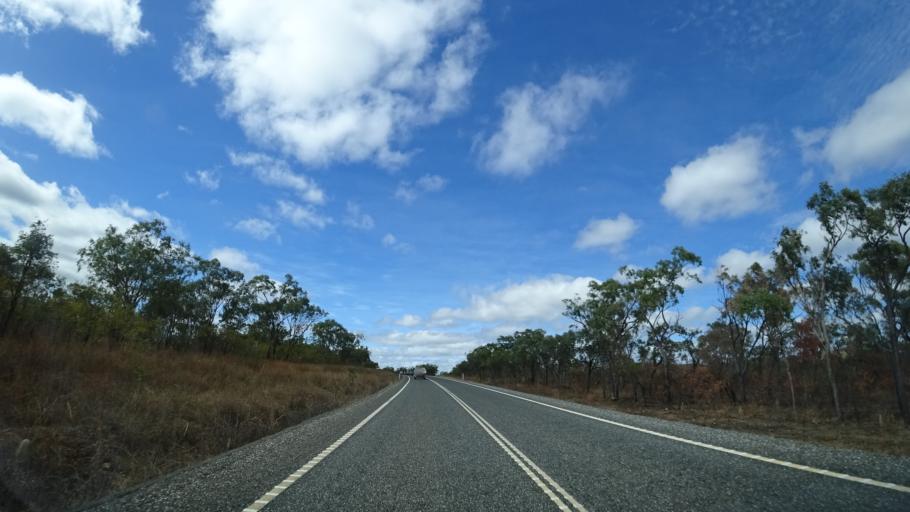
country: AU
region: Queensland
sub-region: Cairns
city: Port Douglas
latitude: -16.4156
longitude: 144.7609
